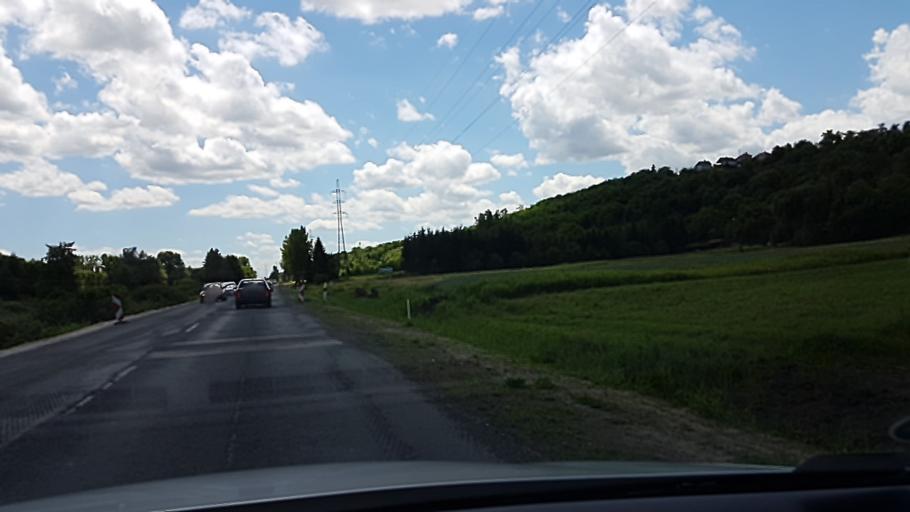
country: HU
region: Zala
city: Zalaegerszeg
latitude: 46.8266
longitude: 16.8633
